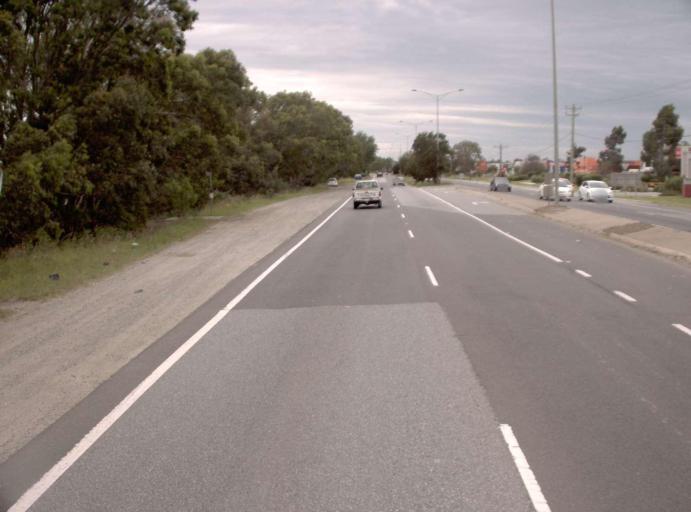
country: AU
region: Victoria
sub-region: Casey
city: Hampton Park
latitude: -38.0182
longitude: 145.2351
